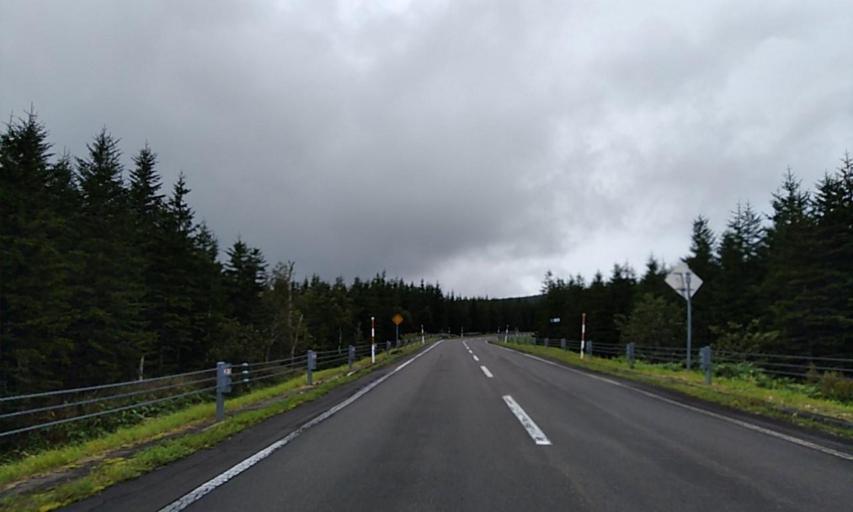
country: JP
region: Hokkaido
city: Abashiri
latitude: 43.6088
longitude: 144.5920
